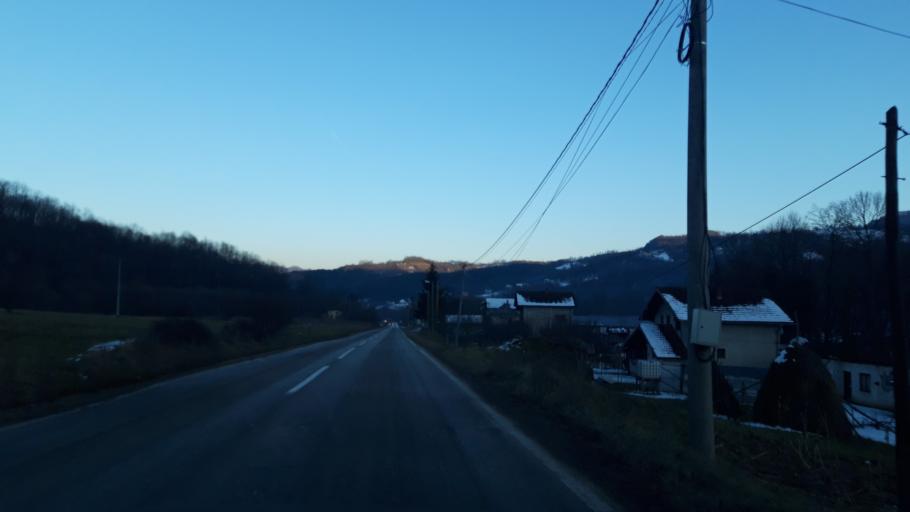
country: BA
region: Republika Srpska
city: Milici
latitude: 44.1644
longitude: 19.0565
